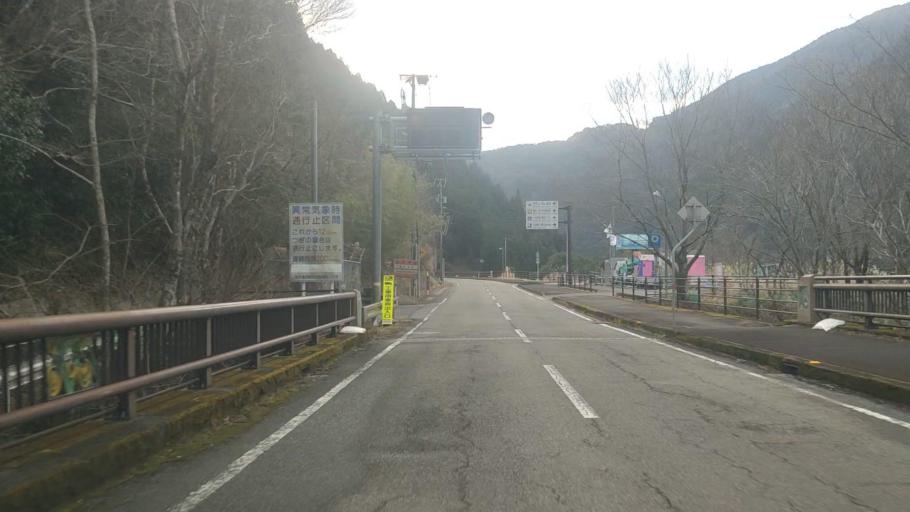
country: JP
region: Kumamoto
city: Hitoyoshi
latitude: 32.3951
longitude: 130.8269
